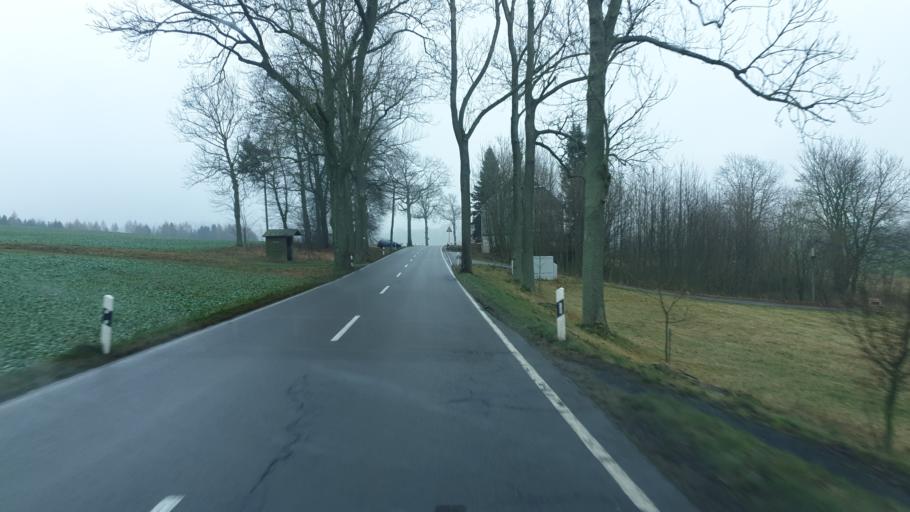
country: DE
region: Saxony
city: Sayda
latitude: 50.7226
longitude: 13.3983
